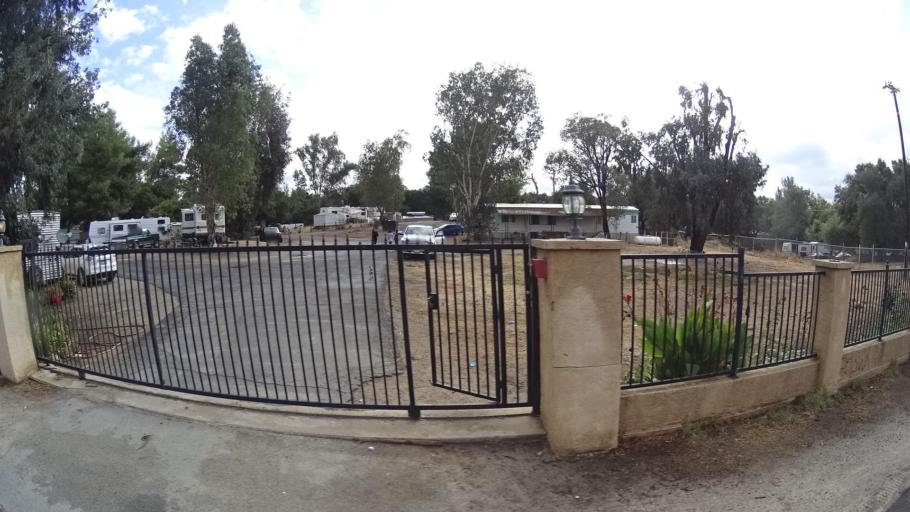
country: MX
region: Baja California
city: Tecate
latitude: 32.6232
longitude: -116.6135
